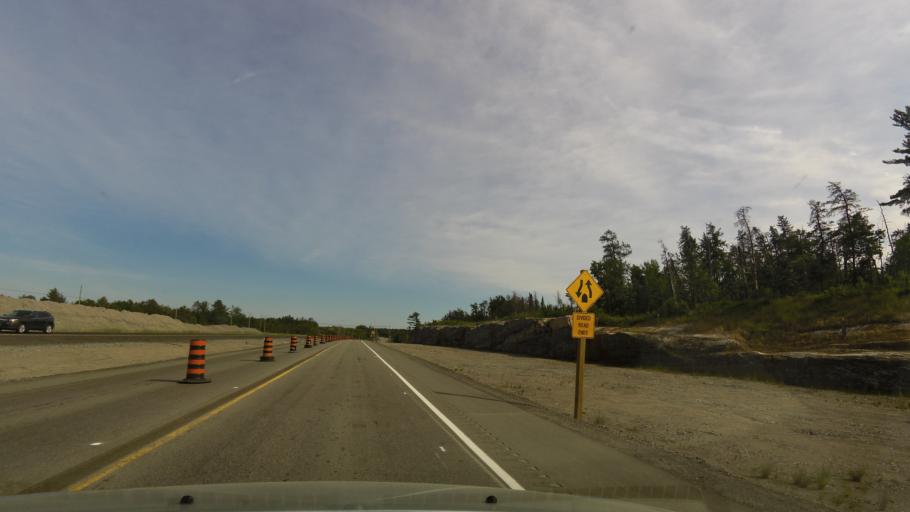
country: CA
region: Ontario
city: Greater Sudbury
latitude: 46.0575
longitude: -80.6255
